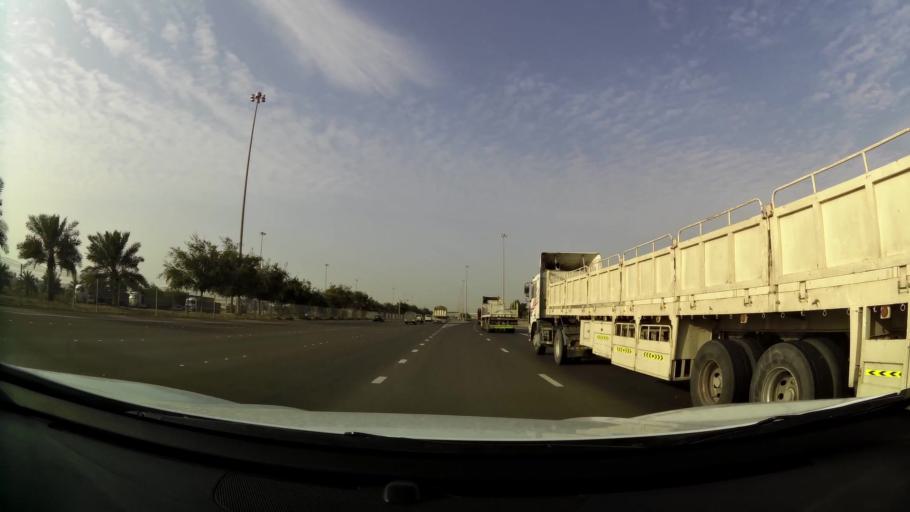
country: AE
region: Abu Dhabi
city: Abu Dhabi
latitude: 24.3172
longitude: 54.5268
